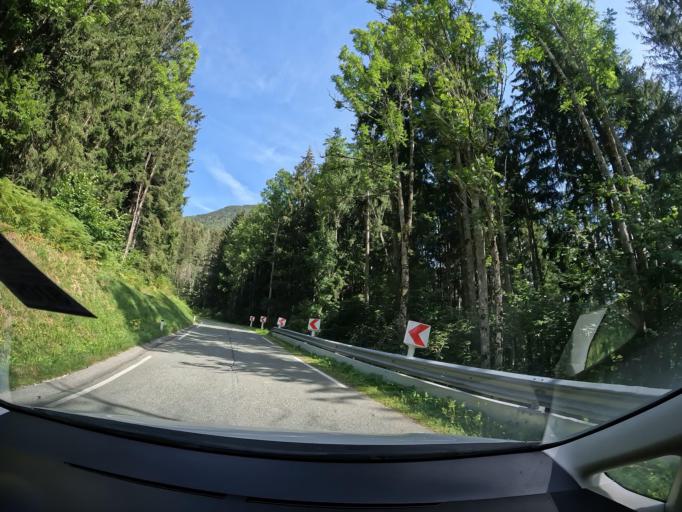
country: AT
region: Carinthia
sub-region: Politischer Bezirk Feldkirchen
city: Glanegg
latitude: 46.7366
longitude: 14.1903
